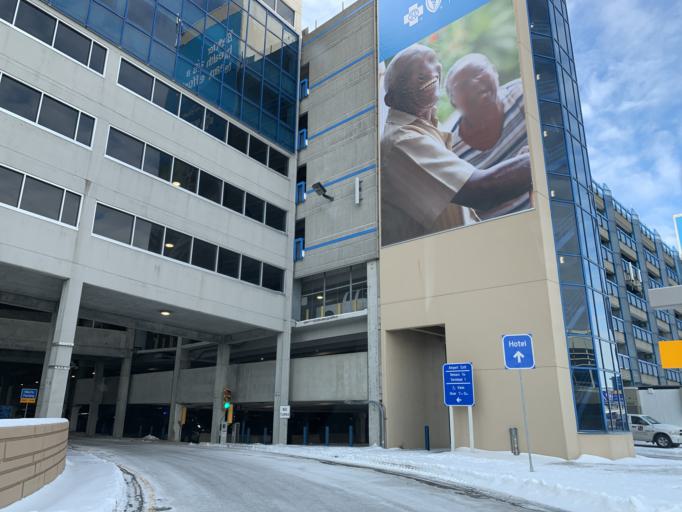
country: US
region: Minnesota
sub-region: Dakota County
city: Mendota Heights
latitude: 44.8829
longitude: -93.2075
